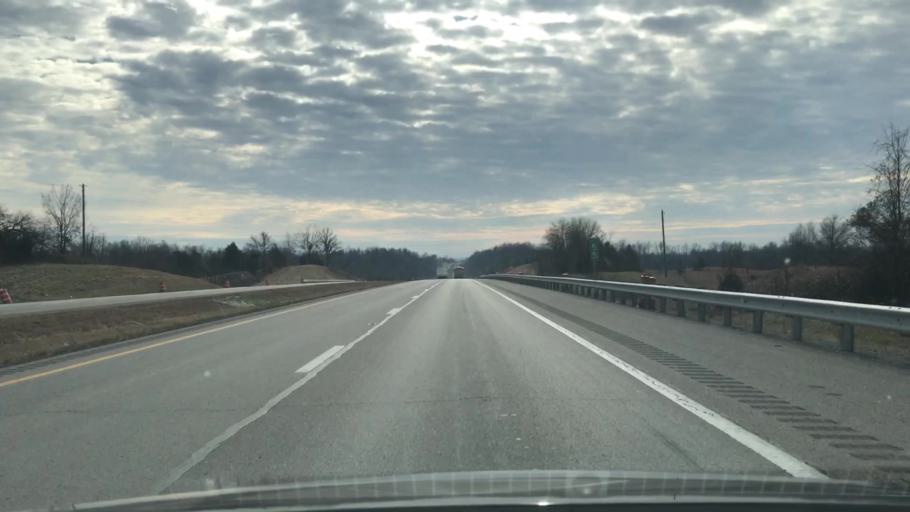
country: US
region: Kentucky
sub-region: Ohio County
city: Hartford
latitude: 37.5237
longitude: -86.9201
